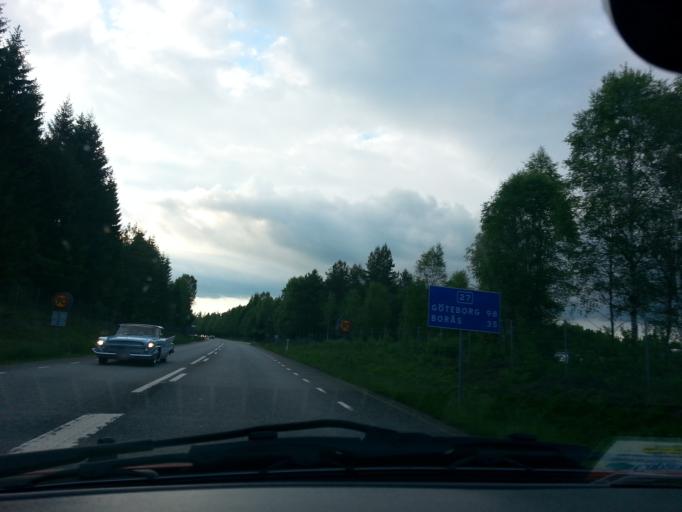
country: SE
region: Vaestra Goetaland
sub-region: Tranemo Kommun
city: Limmared
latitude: 57.5364
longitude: 13.3385
